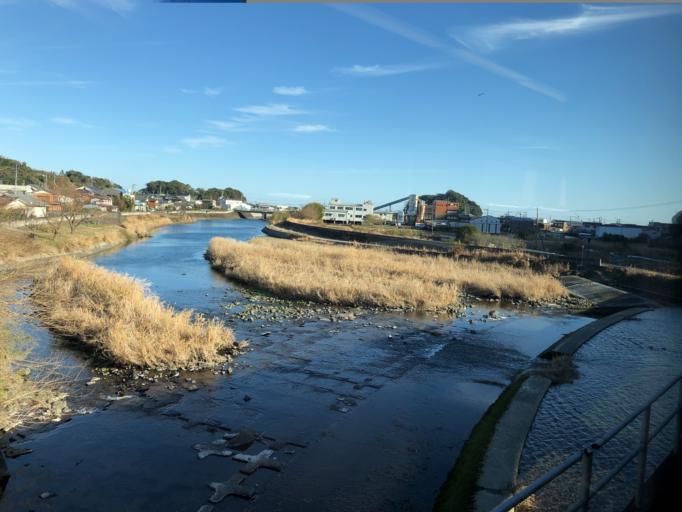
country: JP
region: Kochi
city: Nakamura
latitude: 33.0794
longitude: 133.1018
